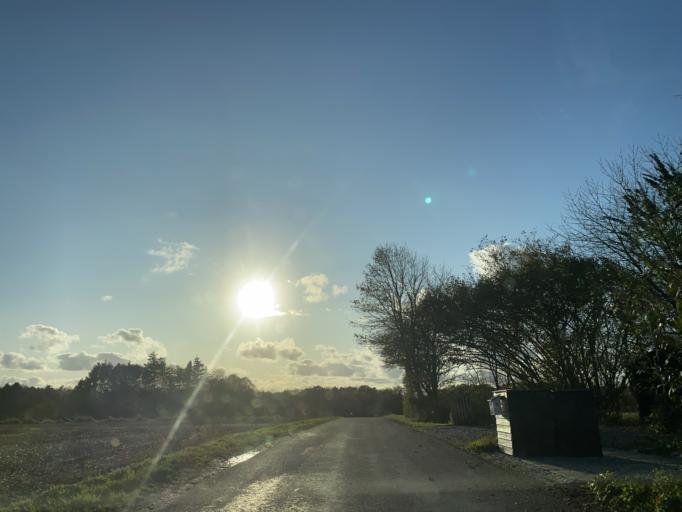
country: DK
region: Central Jutland
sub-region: Viborg Kommune
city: Bjerringbro
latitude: 56.3170
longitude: 9.6978
